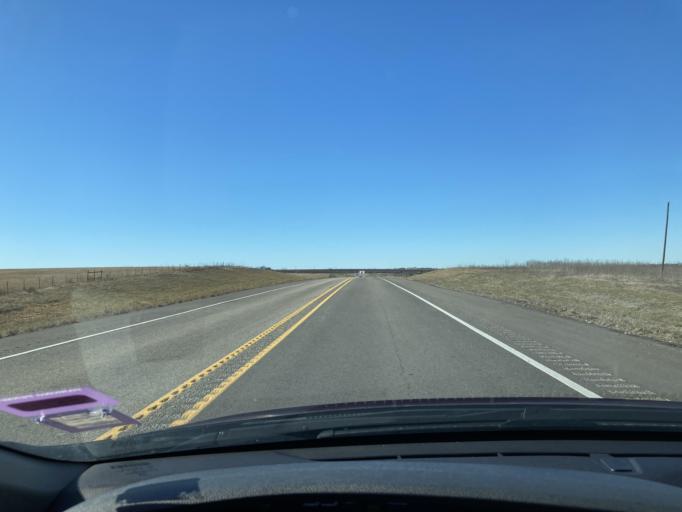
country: US
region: Texas
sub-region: Navarro County
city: Corsicana
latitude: 32.0444
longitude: -96.4366
